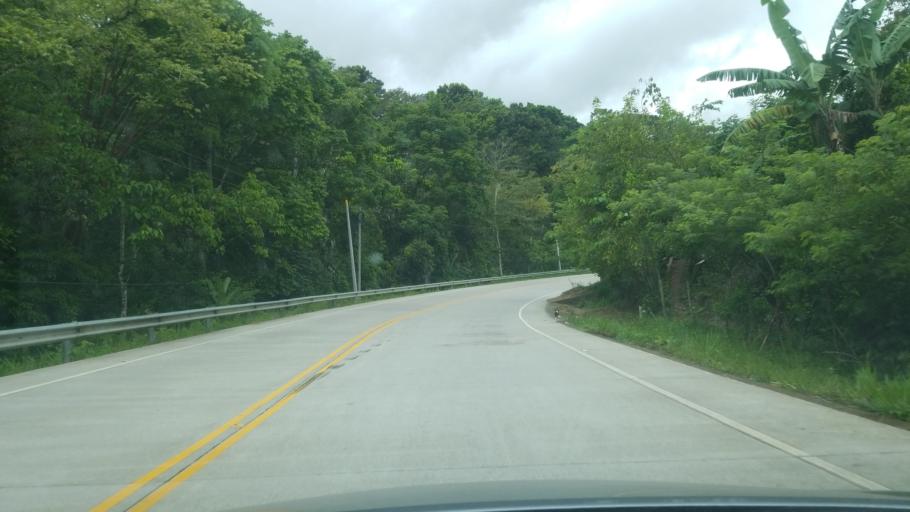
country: HN
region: Copan
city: San Jeronimo
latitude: 14.9477
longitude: -88.9102
